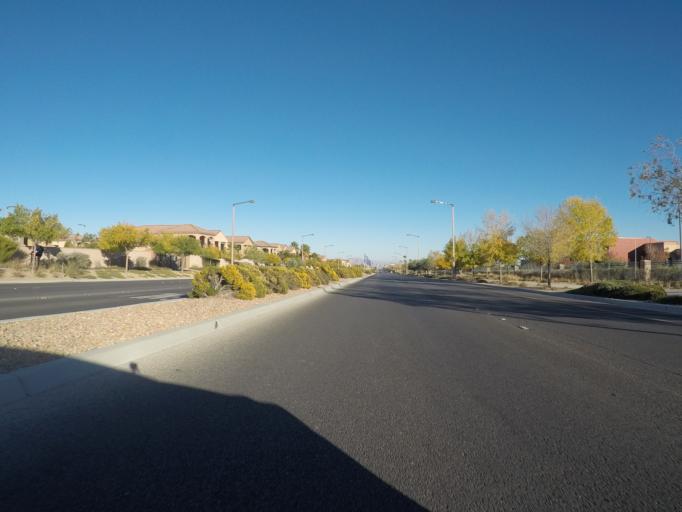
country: US
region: Nevada
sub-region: Clark County
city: Summerlin South
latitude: 36.1589
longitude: -115.3558
